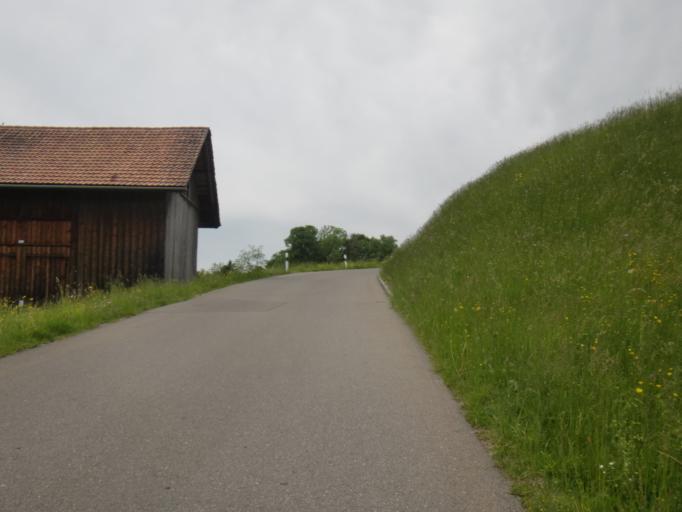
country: CH
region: Zurich
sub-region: Bezirk Hinwil
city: Wald
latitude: 47.2781
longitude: 8.9029
